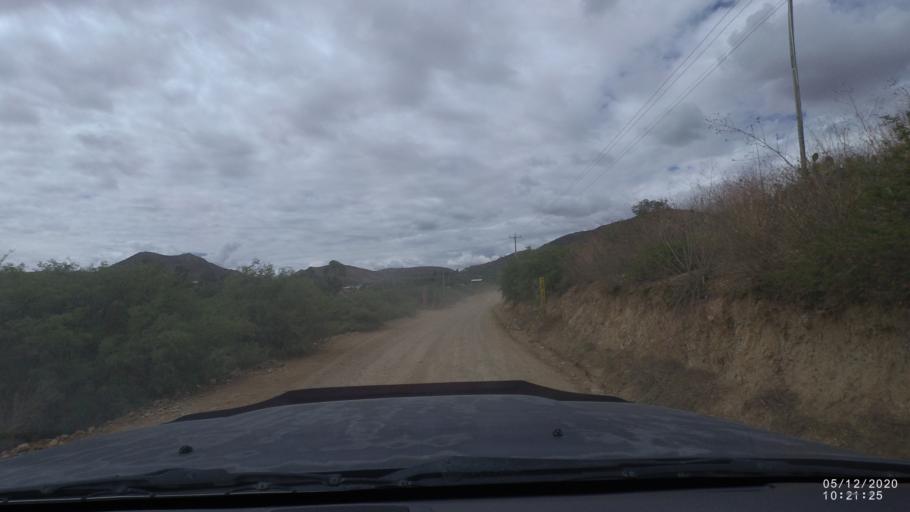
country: BO
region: Cochabamba
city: Sipe Sipe
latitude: -17.4899
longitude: -66.2819
